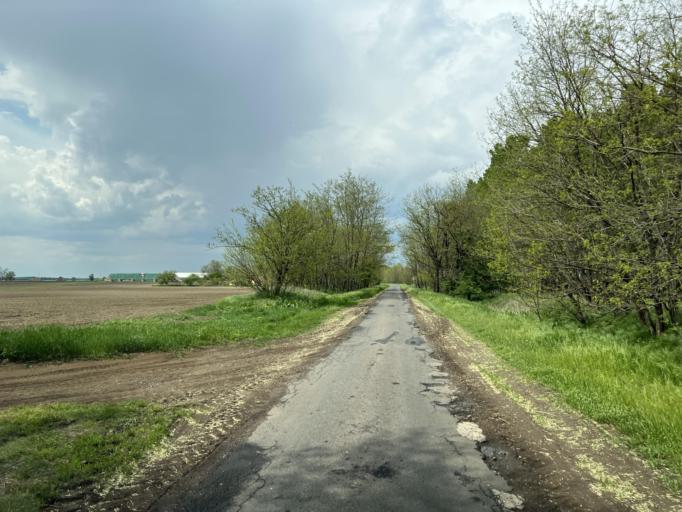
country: HU
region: Pest
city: Nagykoros
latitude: 46.9743
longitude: 19.8152
